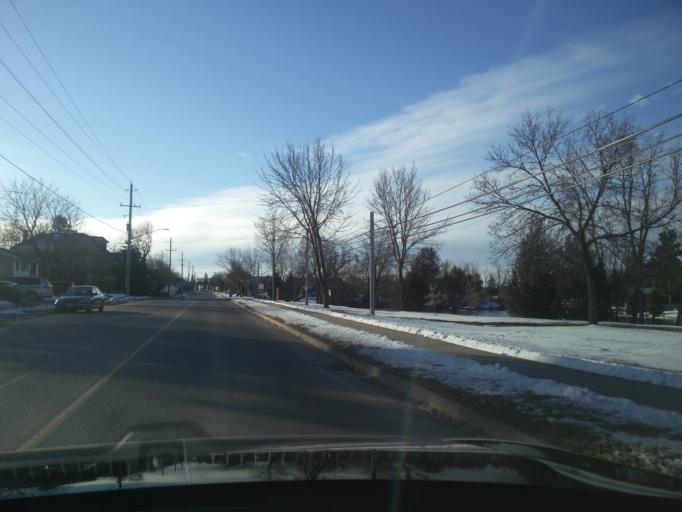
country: CA
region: Ontario
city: Gananoque
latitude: 44.3346
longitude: -76.1681
